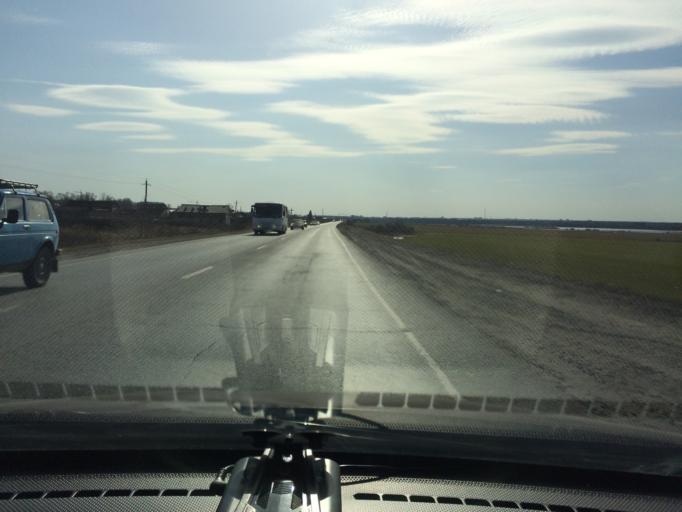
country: RU
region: Mariy-El
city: Yoshkar-Ola
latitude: 56.6654
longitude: 47.9893
